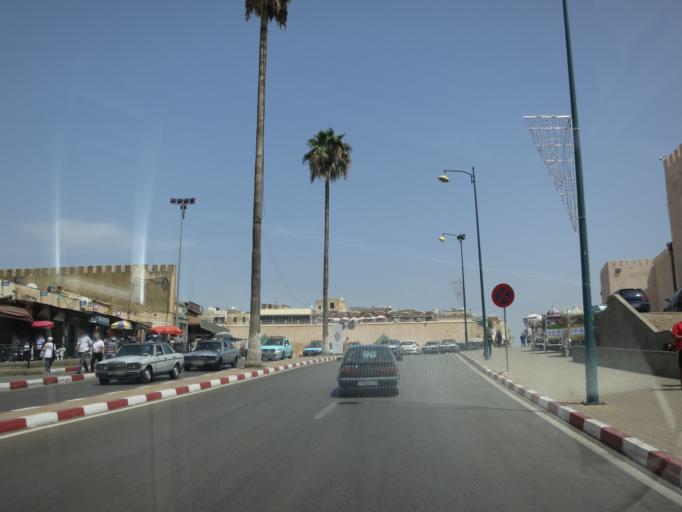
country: MA
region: Meknes-Tafilalet
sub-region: Meknes
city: Meknes
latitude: 33.8921
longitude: -5.5660
